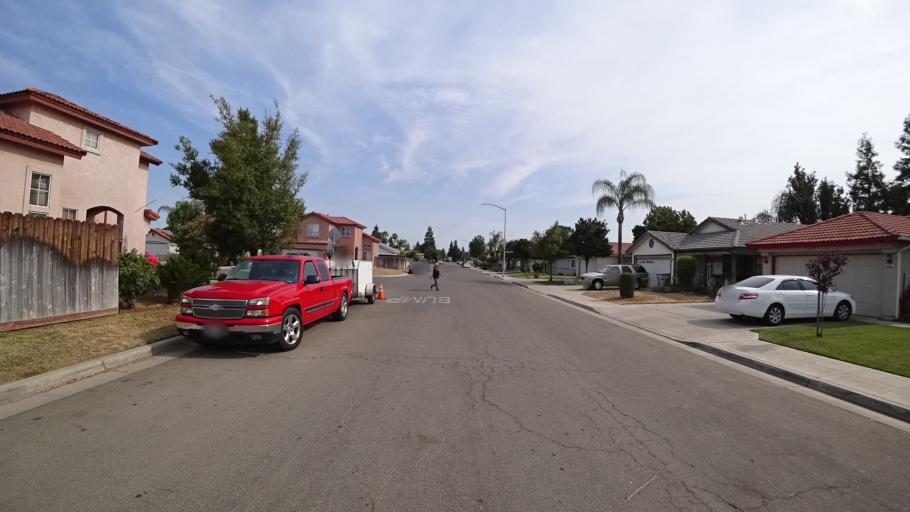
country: US
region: California
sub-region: Fresno County
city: West Park
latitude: 36.7690
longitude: -119.8673
